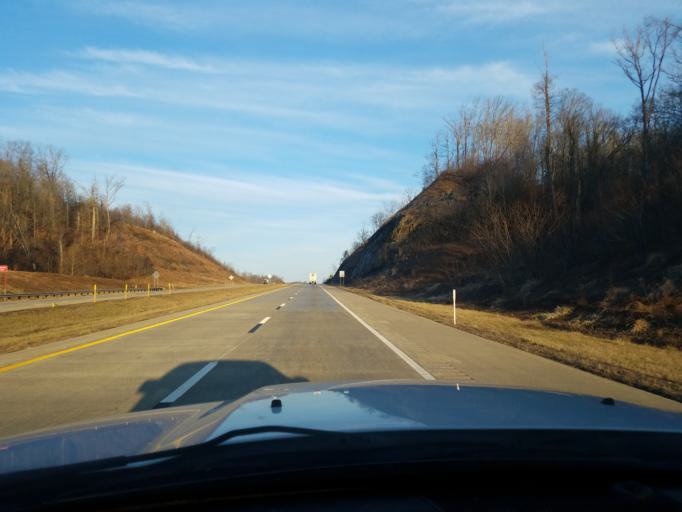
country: US
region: West Virginia
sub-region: Putnam County
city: Eleanor
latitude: 38.5263
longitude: -81.9392
